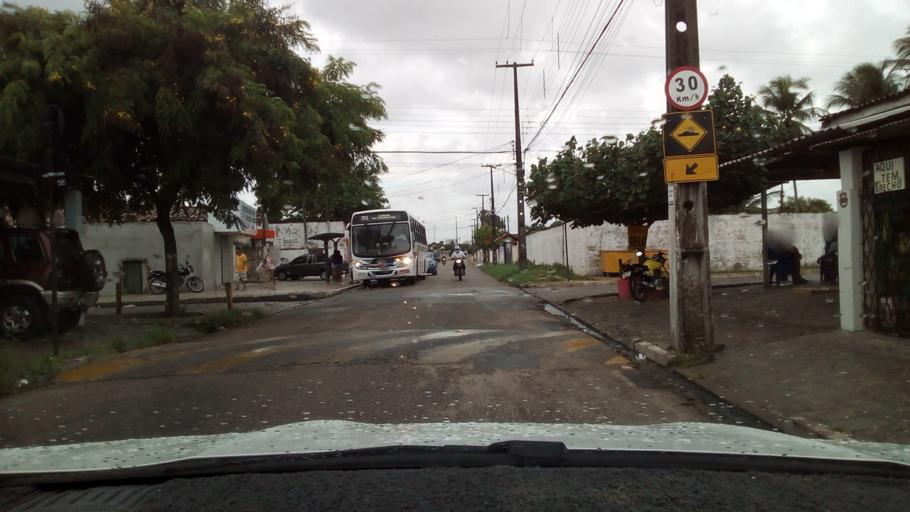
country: BR
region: Paraiba
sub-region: Joao Pessoa
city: Joao Pessoa
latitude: -7.1492
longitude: -34.8716
